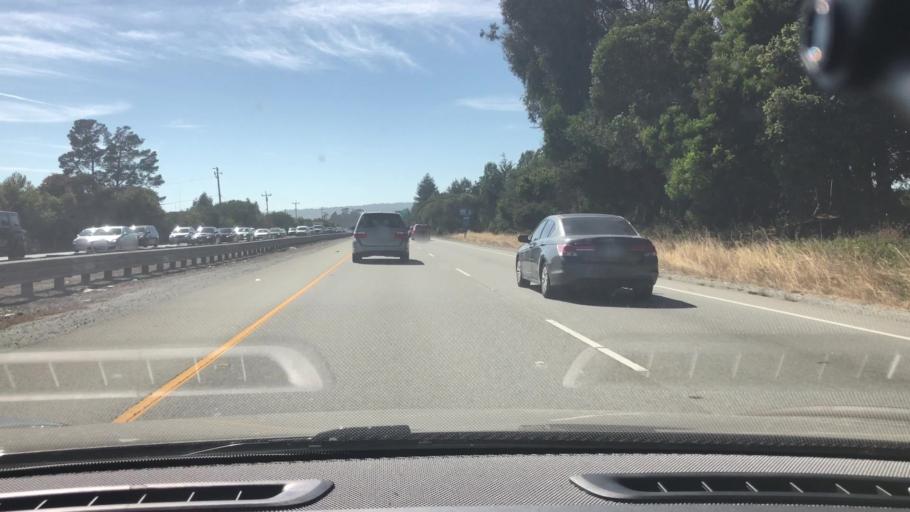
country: US
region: California
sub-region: Santa Cruz County
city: Live Oak
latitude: 36.9848
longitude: -121.9750
